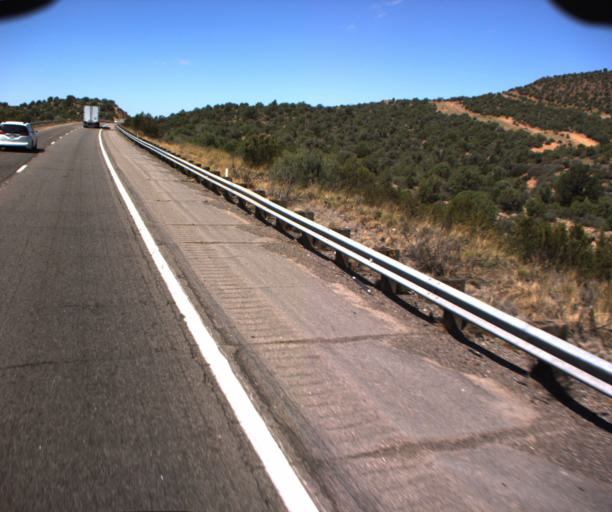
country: US
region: Arizona
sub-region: Mohave County
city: Peach Springs
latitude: 35.1819
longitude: -113.4728
